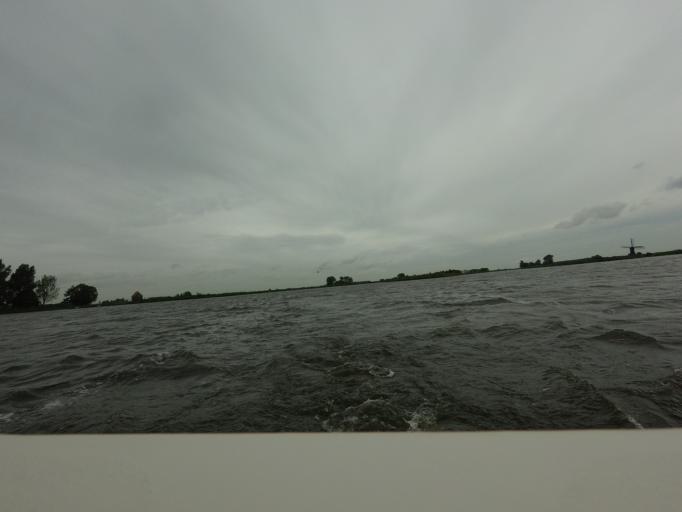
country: NL
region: Friesland
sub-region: Gemeente Boarnsterhim
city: Grou
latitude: 53.1075
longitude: 5.8579
